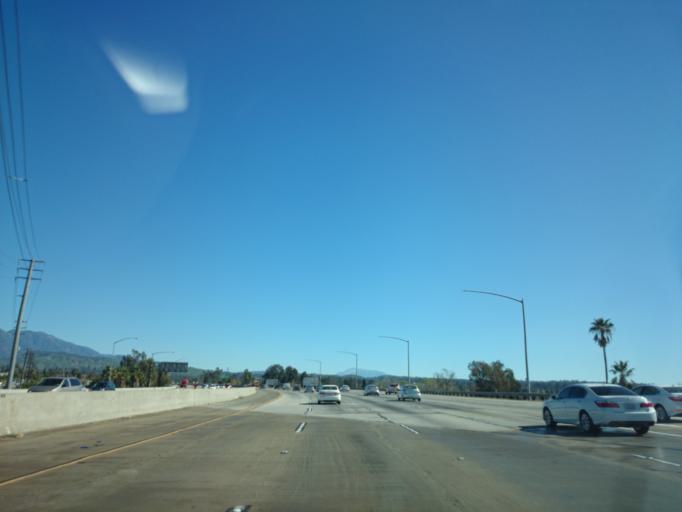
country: US
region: California
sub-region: San Bernardino County
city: Redlands
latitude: 34.0628
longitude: -117.1957
